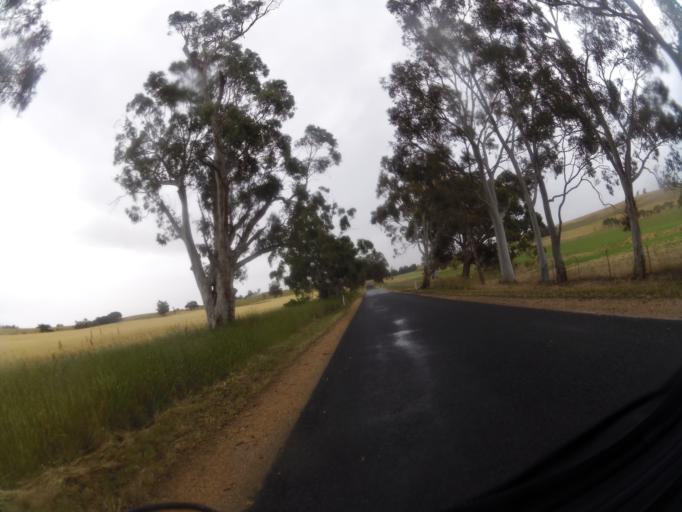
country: AU
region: Victoria
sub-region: Mount Alexander
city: Castlemaine
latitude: -37.2515
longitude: 144.0297
